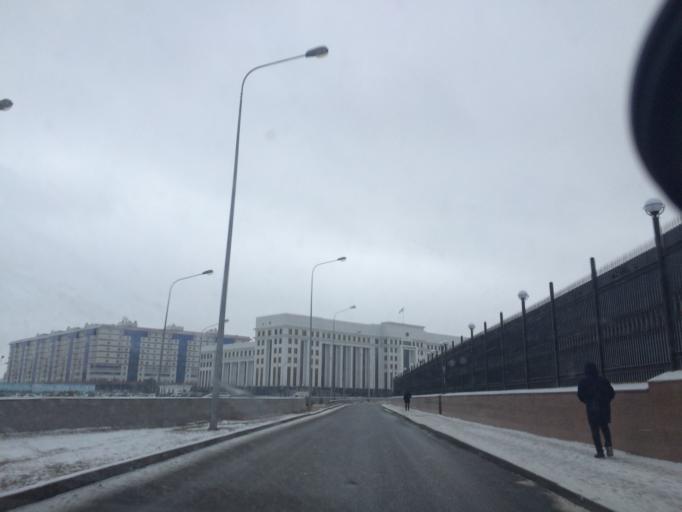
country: KZ
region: Astana Qalasy
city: Astana
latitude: 51.1218
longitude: 71.4348
